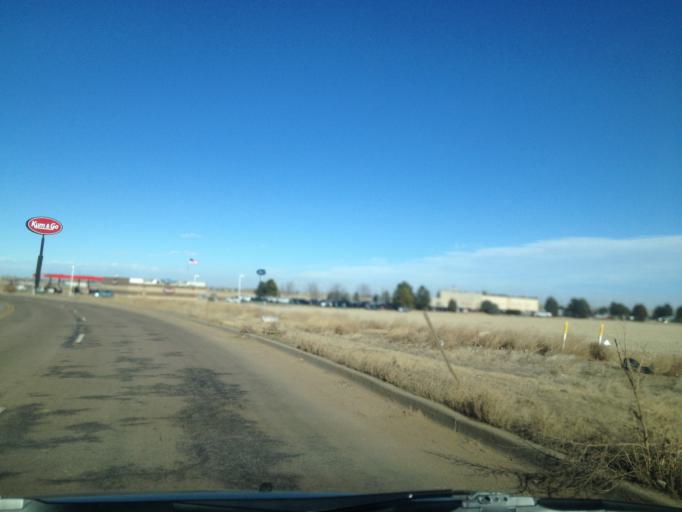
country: US
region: Colorado
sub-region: Weld County
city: Dacono
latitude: 40.0853
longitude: -104.9754
